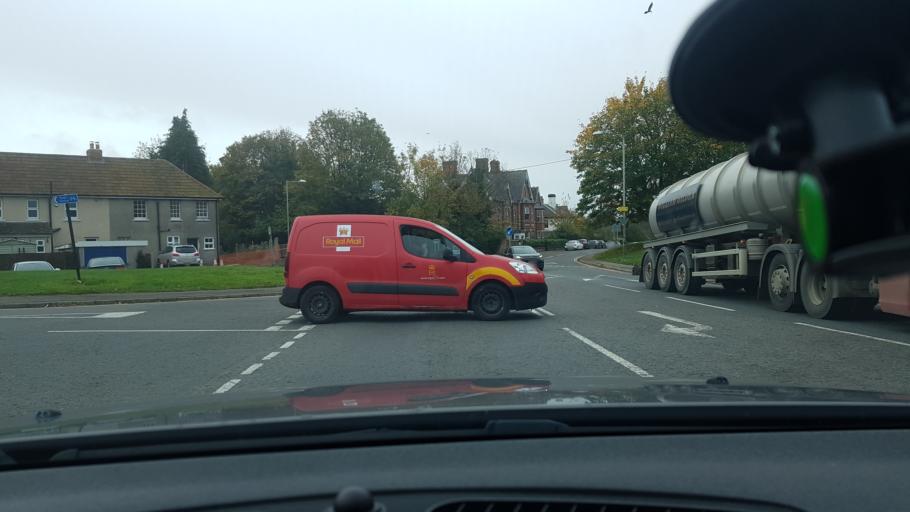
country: GB
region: England
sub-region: Wiltshire
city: Marlborough
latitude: 51.4258
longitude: -1.7307
